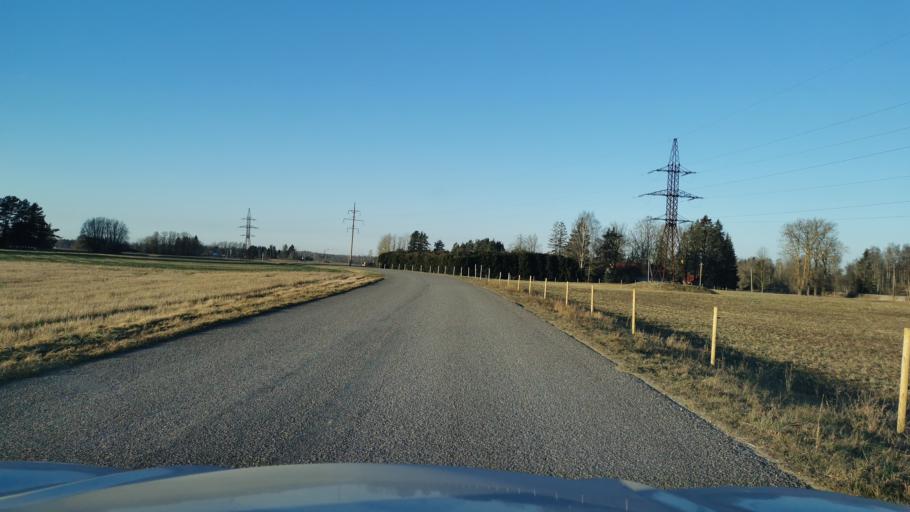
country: EE
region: Ida-Virumaa
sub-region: Puessi linn
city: Pussi
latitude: 59.3430
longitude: 27.0465
